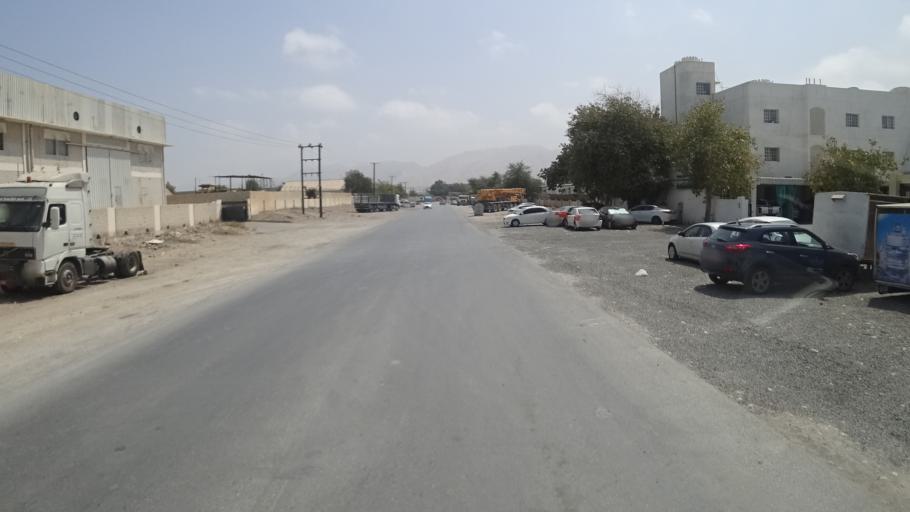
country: OM
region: Muhafazat Masqat
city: Bawshar
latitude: 23.5768
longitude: 58.3717
